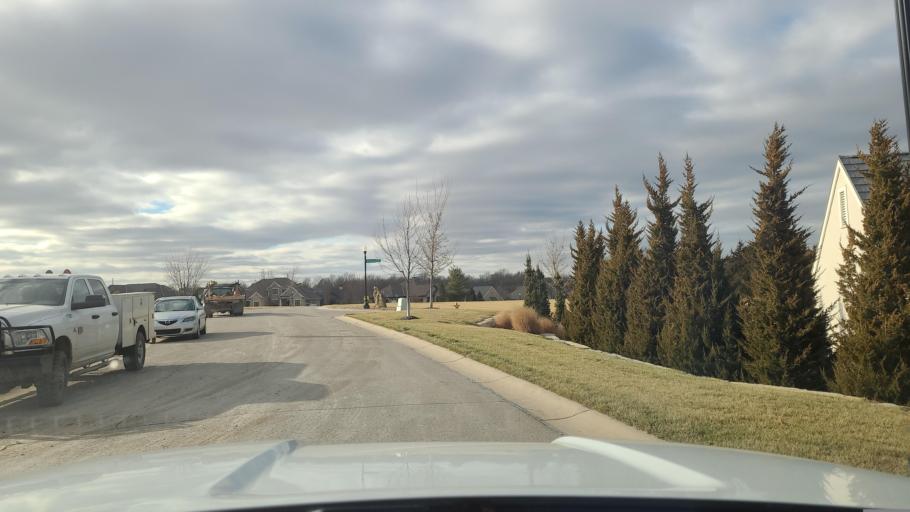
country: US
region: Kansas
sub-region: Douglas County
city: Lawrence
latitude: 38.9809
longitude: -95.2844
